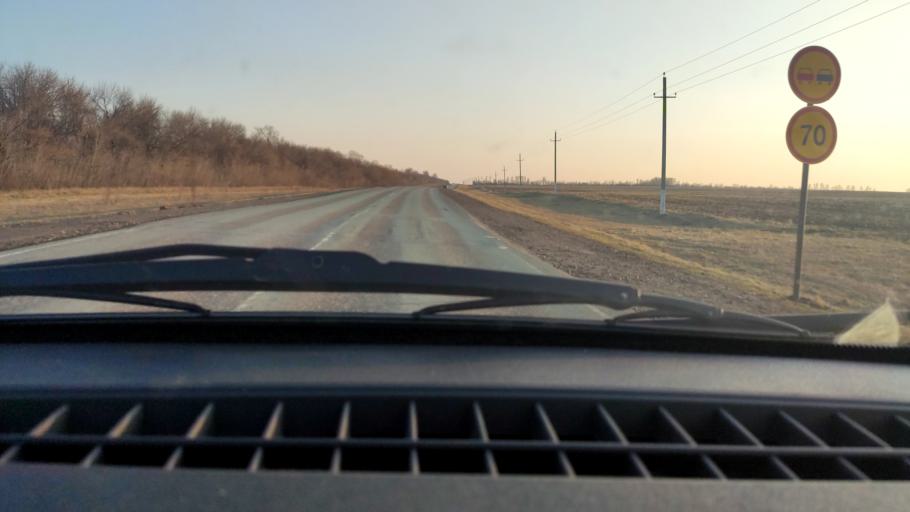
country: RU
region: Bashkortostan
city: Davlekanovo
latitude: 54.3286
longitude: 55.1646
